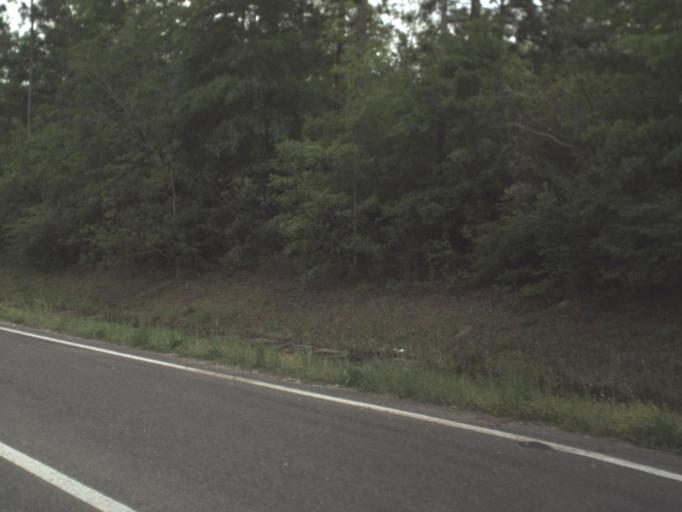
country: US
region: Florida
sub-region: Escambia County
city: Cantonment
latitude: 30.6472
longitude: -87.3492
